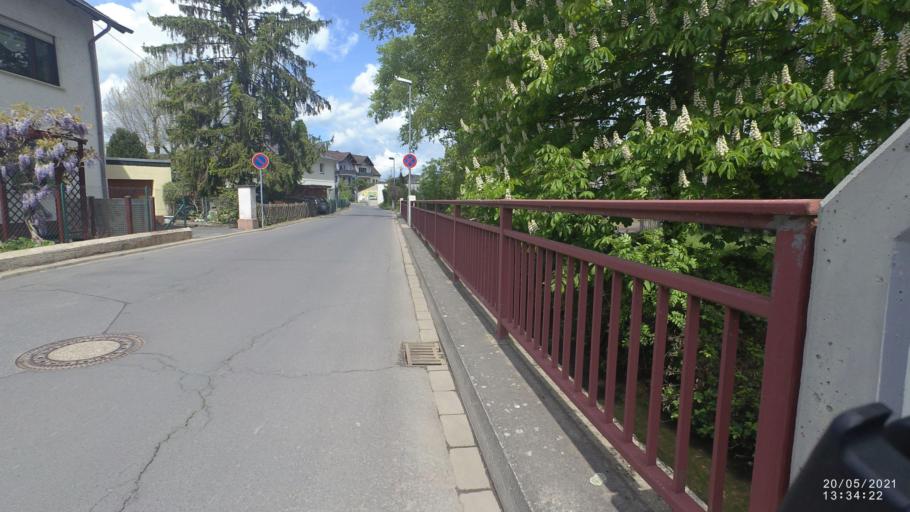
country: DE
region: Rheinland-Pfalz
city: Saffig
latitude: 50.4000
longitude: 7.4140
